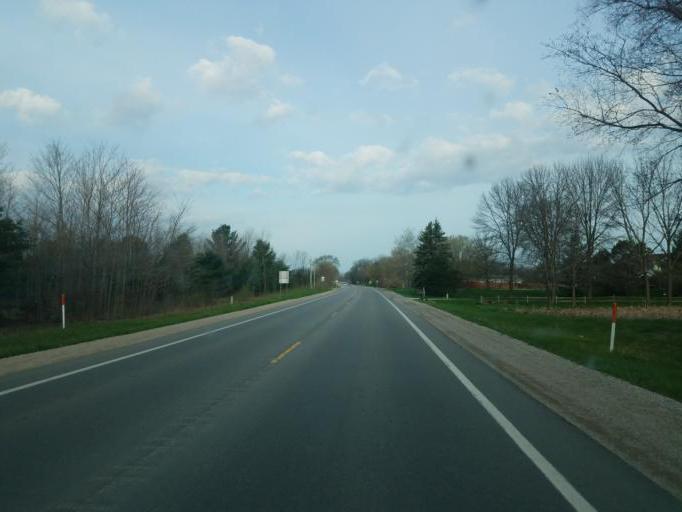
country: US
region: Michigan
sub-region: Isabella County
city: Mount Pleasant
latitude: 43.5977
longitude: -84.8653
